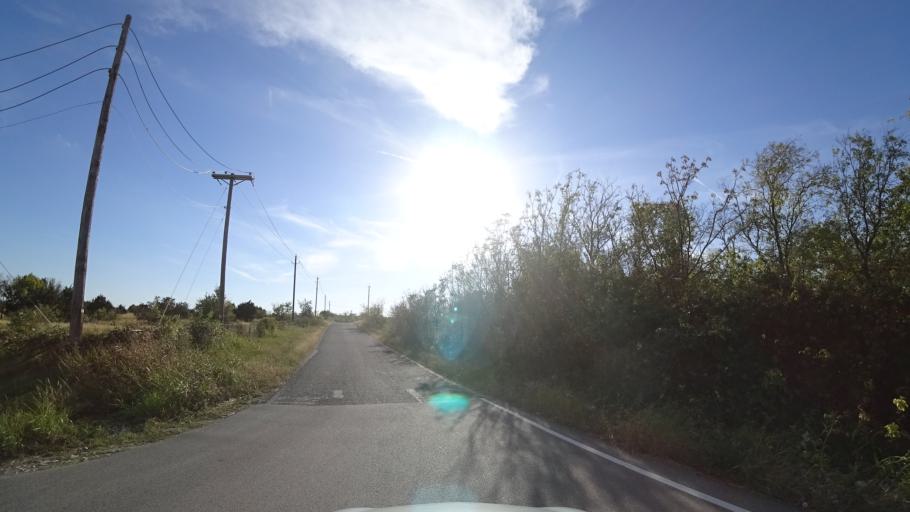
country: US
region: Texas
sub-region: Travis County
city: Wells Branch
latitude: 30.4504
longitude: -97.6984
